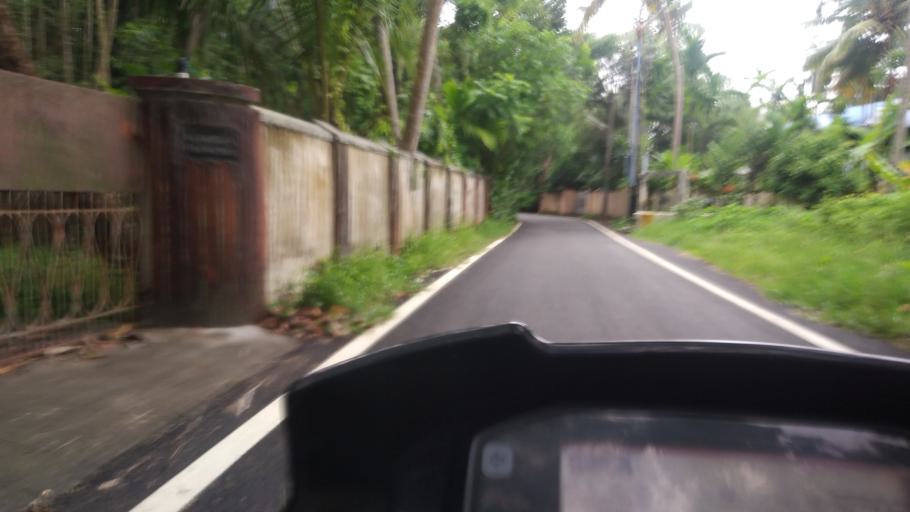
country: IN
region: Kerala
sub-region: Ernakulam
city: Elur
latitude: 10.0584
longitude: 76.2262
